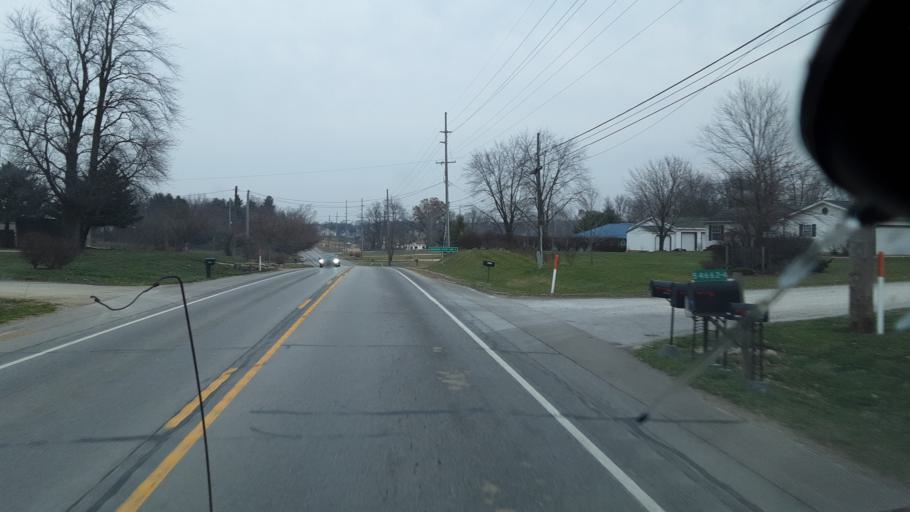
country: US
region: Indiana
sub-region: Elkhart County
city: Middlebury
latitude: 41.7012
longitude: -85.6898
